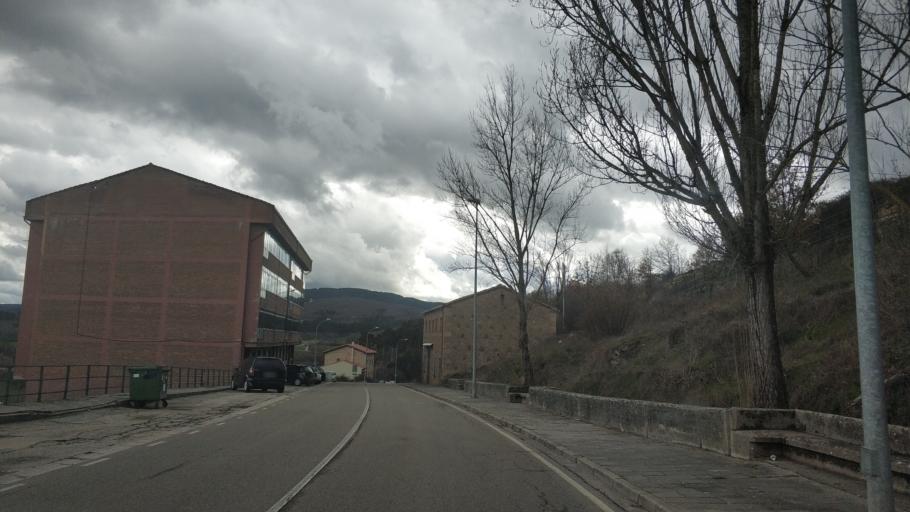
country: ES
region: Castille and Leon
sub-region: Provincia de Burgos
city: Quintanar de la Sierra
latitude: 41.9771
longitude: -3.0439
